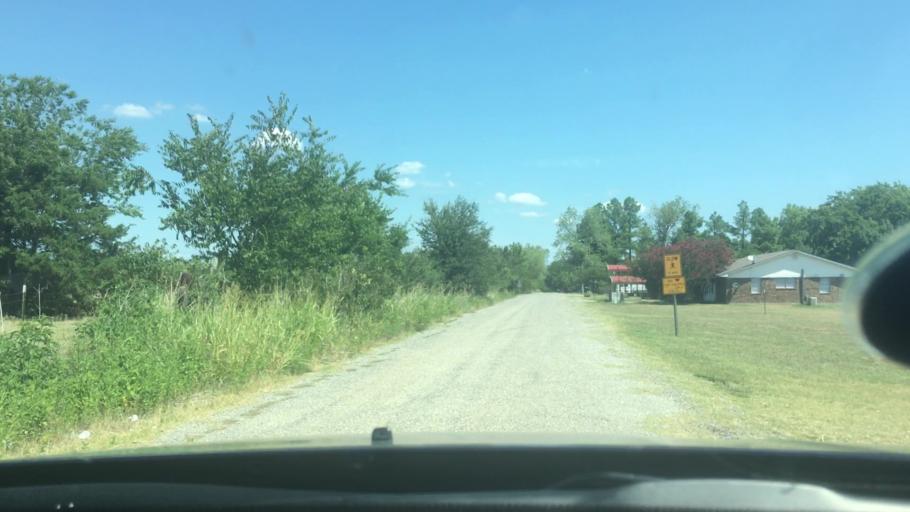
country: US
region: Oklahoma
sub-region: Bryan County
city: Colbert
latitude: 33.8535
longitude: -96.4926
